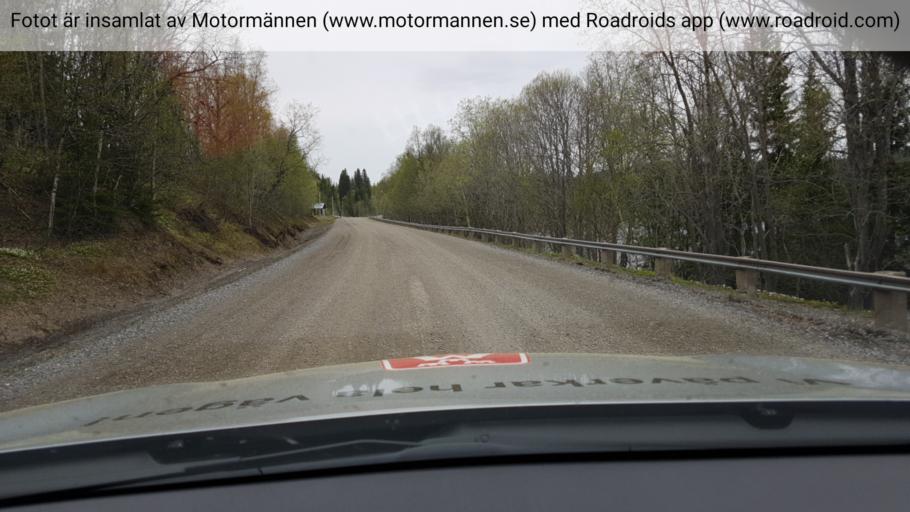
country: SE
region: Jaemtland
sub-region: Are Kommun
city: Are
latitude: 63.7107
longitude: 12.6350
